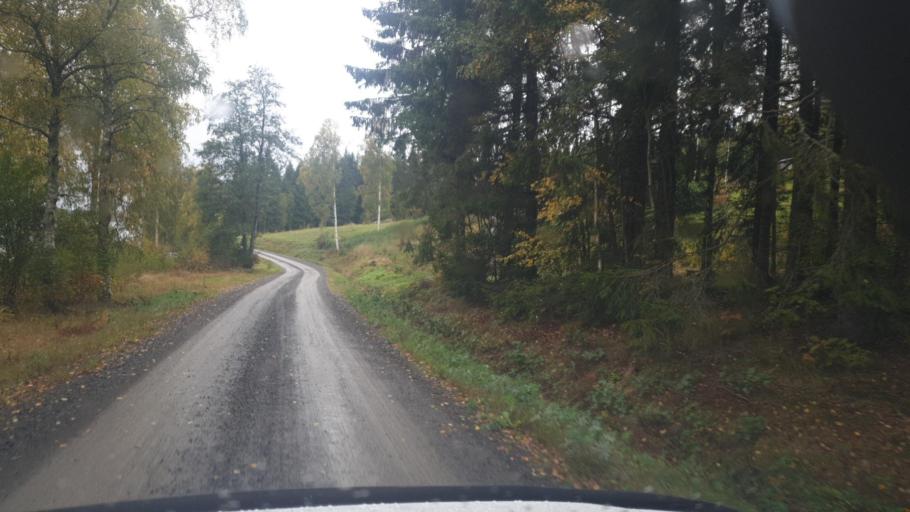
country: SE
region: Vaermland
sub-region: Arvika Kommun
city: Arvika
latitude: 59.8635
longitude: 12.8249
